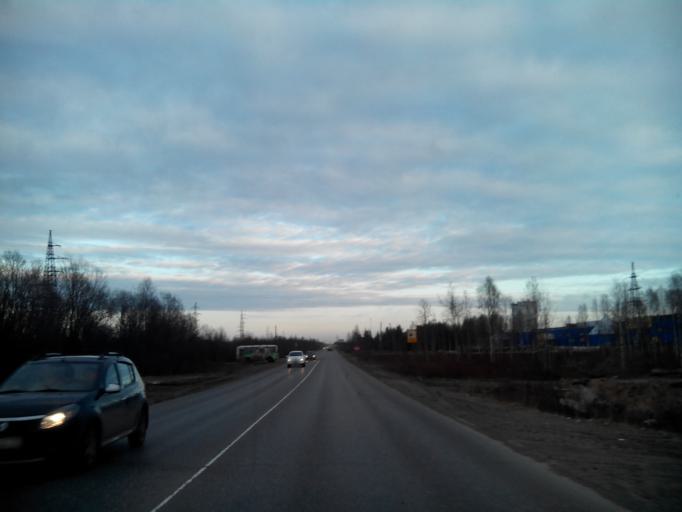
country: RU
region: Arkhangelskaya
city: Arkhangel'sk
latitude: 64.5315
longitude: 40.6502
